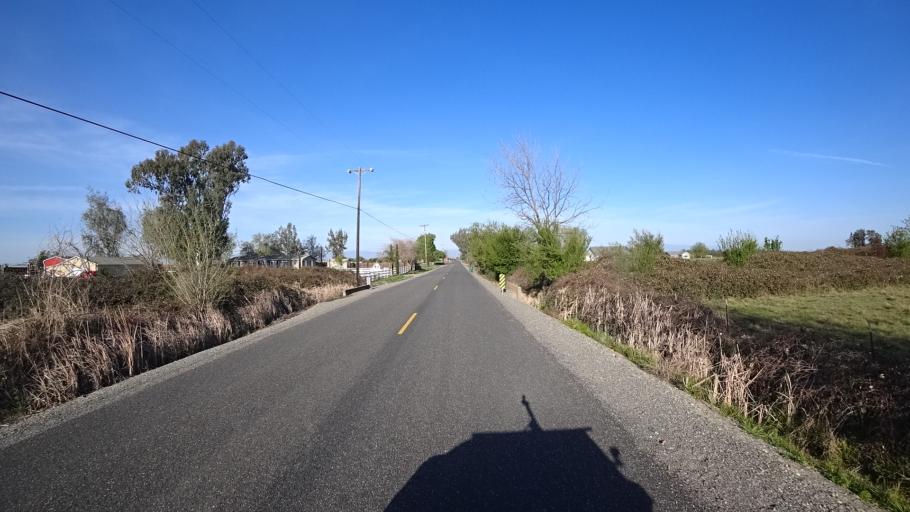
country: US
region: California
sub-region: Glenn County
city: Orland
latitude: 39.7260
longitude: -122.2229
